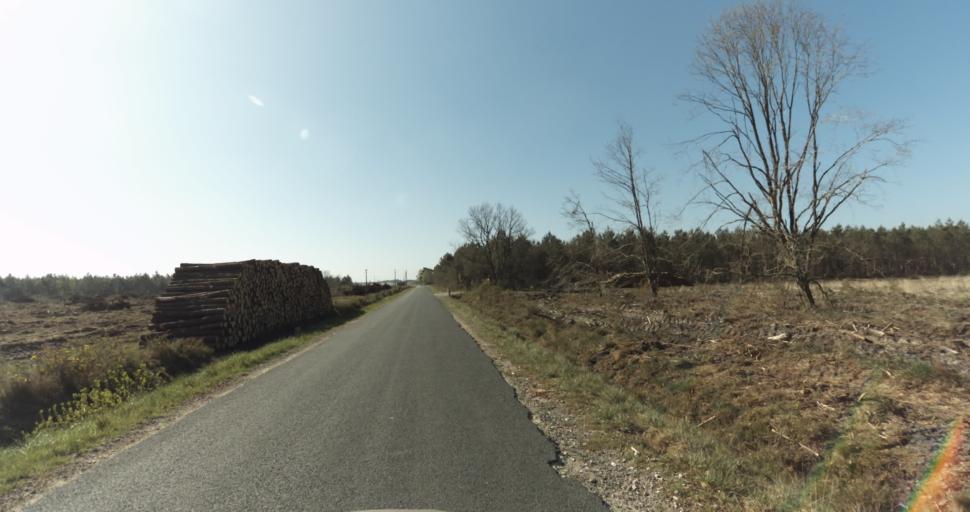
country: FR
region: Aquitaine
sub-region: Departement de la Gironde
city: Marcheprime
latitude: 44.7777
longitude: -0.8596
